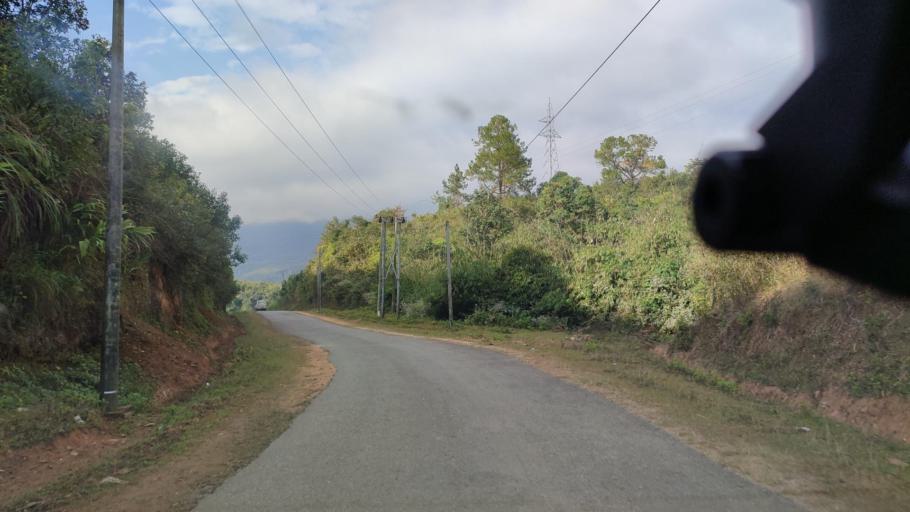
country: TH
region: Chiang Rai
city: Mae Sai
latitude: 21.1958
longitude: 99.6006
